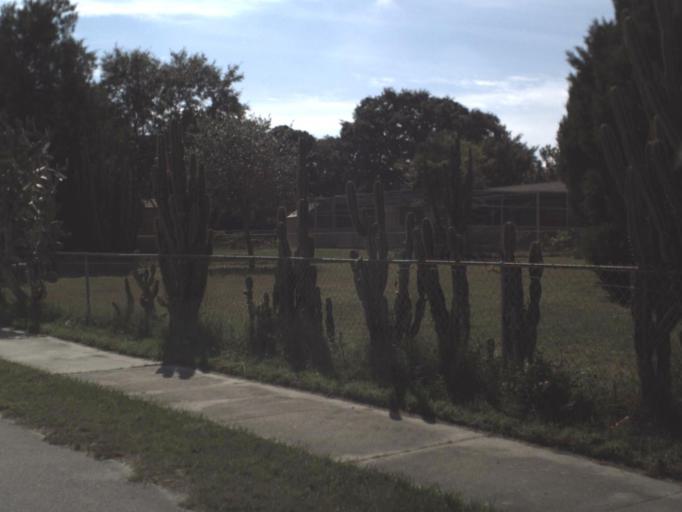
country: US
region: Florida
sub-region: Highlands County
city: Sebring
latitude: 27.5081
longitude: -81.4425
